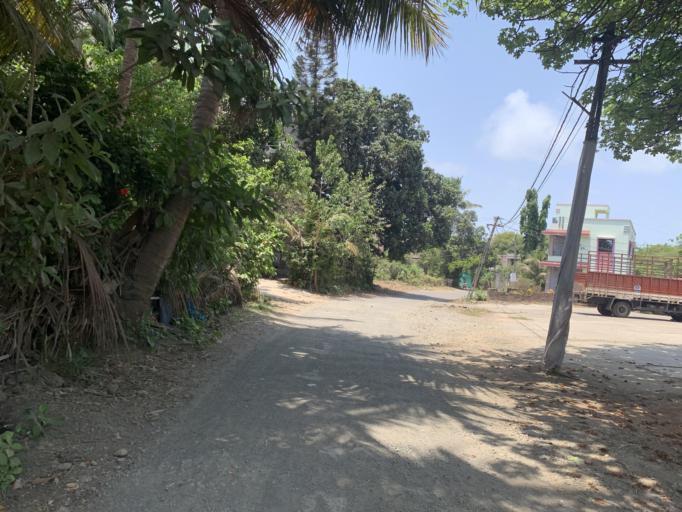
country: IN
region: Daman and Diu
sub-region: Daman District
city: Daman
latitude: 20.4548
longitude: 72.8485
